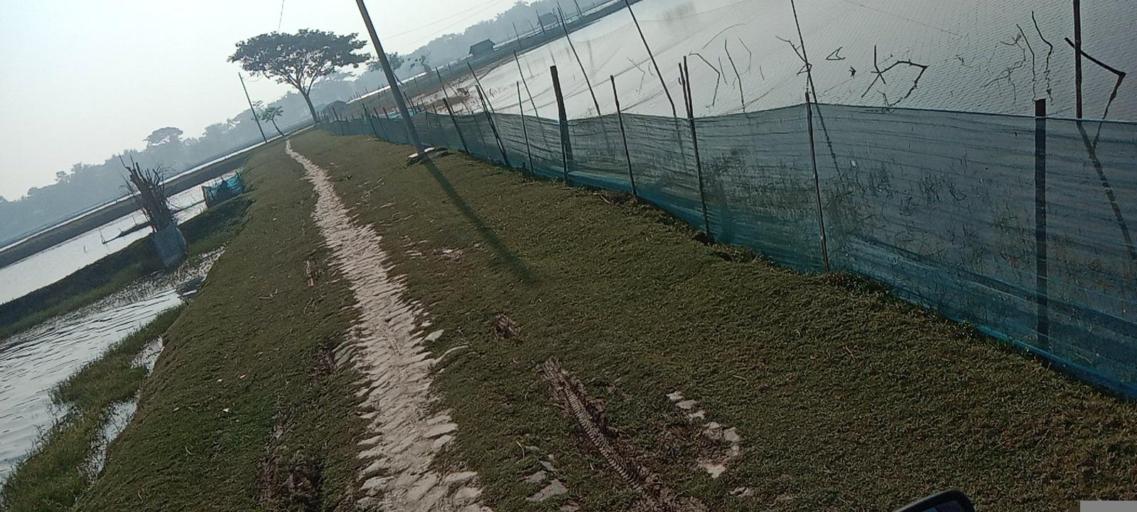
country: BD
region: Khulna
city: Phultala
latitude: 22.6107
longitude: 89.5848
